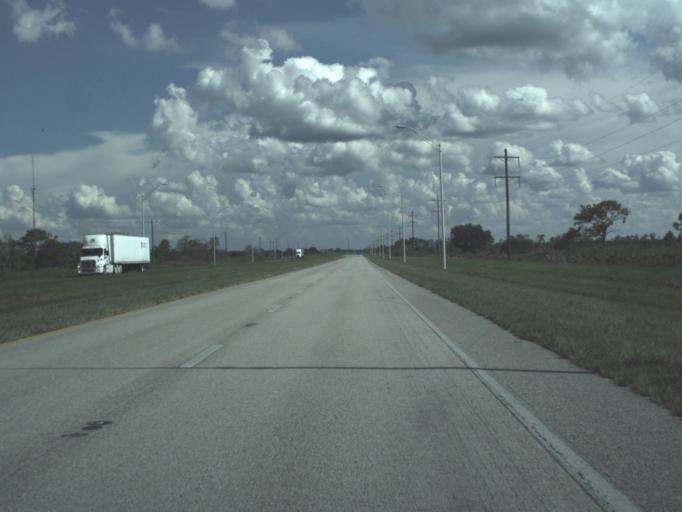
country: US
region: Florida
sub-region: Polk County
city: Babson Park
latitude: 27.8568
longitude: -81.3727
